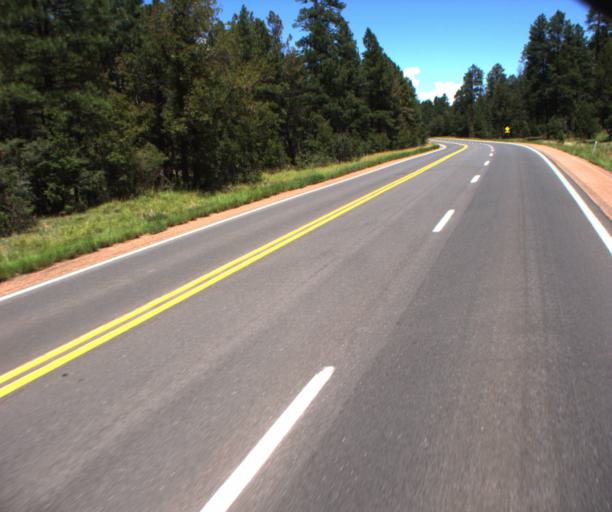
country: US
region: Arizona
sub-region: Navajo County
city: Show Low
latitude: 34.1837
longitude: -110.0932
